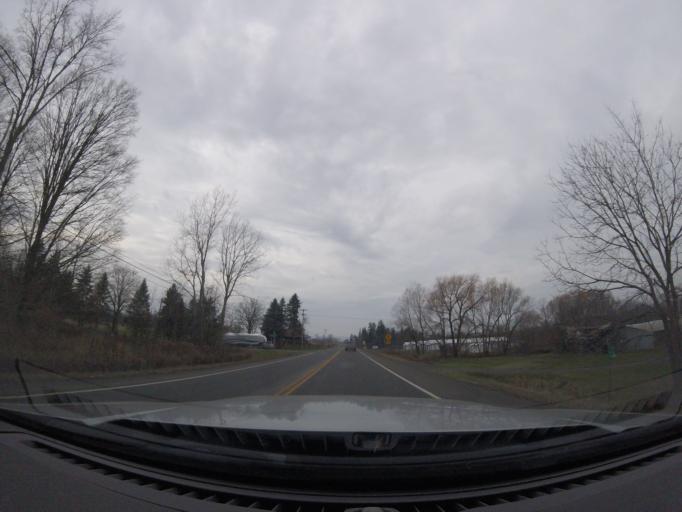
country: US
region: New York
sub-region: Schuyler County
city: Watkins Glen
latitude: 42.4241
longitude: -76.8168
